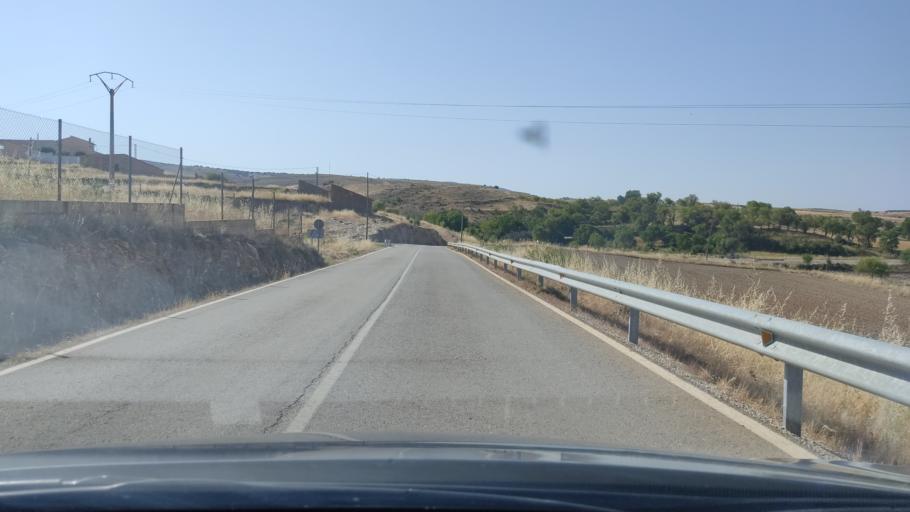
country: ES
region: Aragon
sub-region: Provincia de Teruel
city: Cucalon
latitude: 41.0865
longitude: -1.2187
